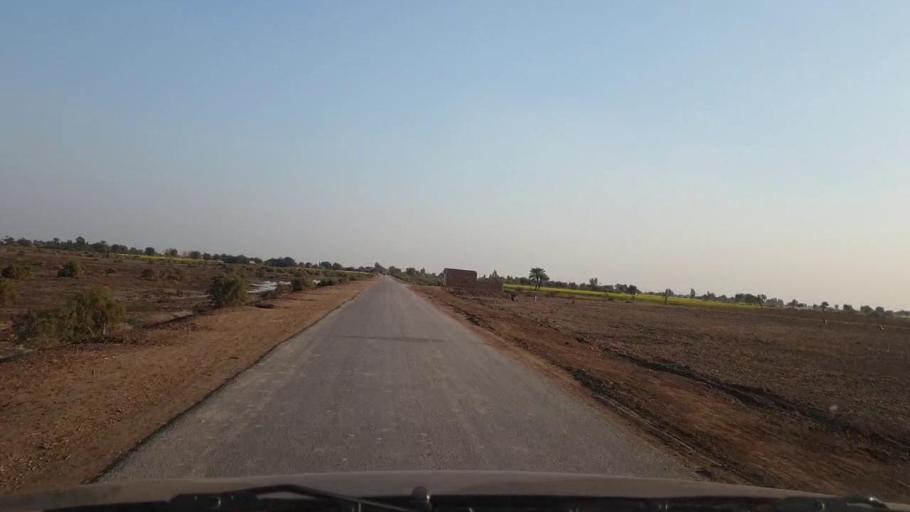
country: PK
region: Sindh
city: Jhol
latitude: 25.9349
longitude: 68.9149
